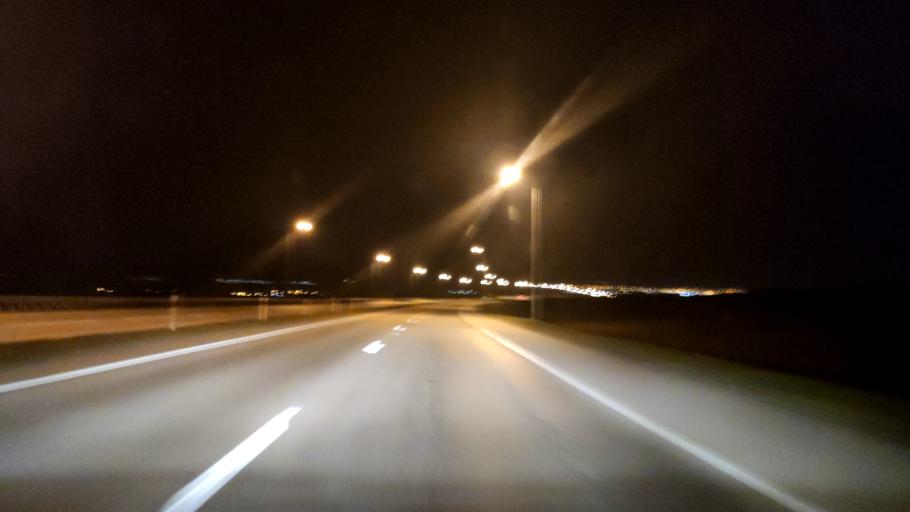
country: RU
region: Belgorod
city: Staryy Oskol
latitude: 51.3369
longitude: 37.7670
